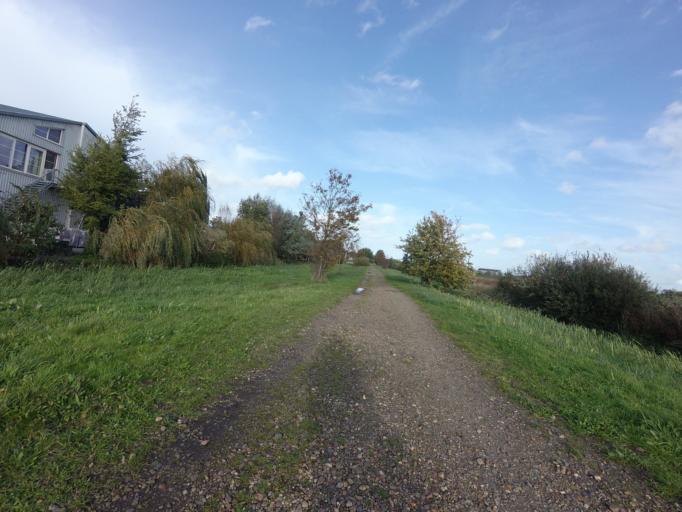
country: NL
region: Utrecht
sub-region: Gemeente De Ronde Venen
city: Mijdrecht
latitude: 52.2035
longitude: 4.9221
